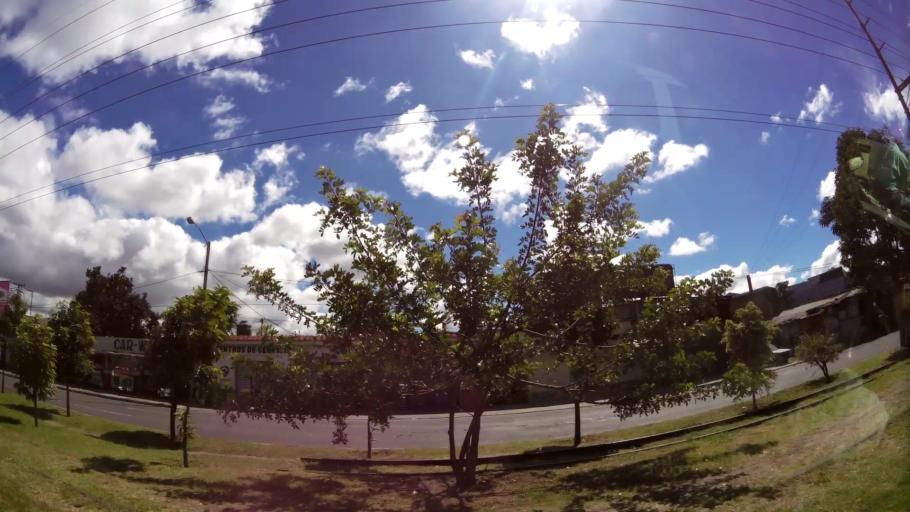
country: GT
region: Guatemala
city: Guatemala City
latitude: 14.6053
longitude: -90.5352
